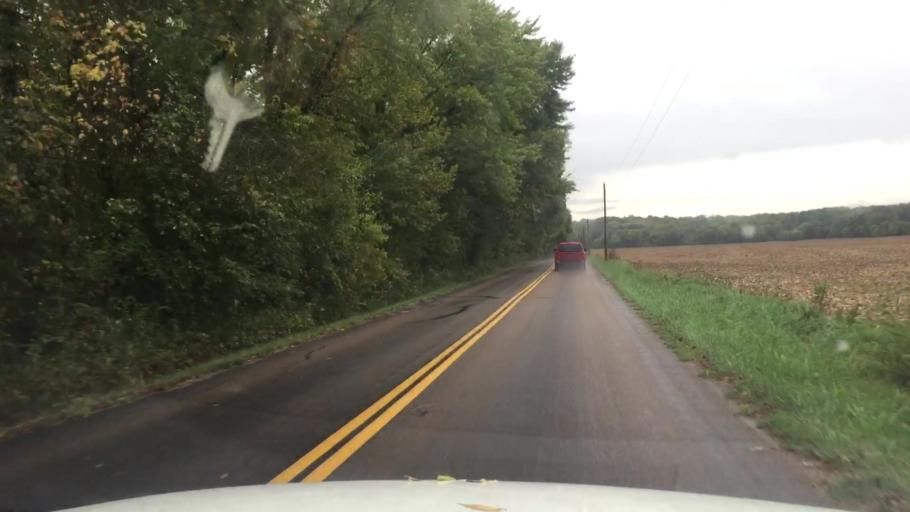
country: US
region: Missouri
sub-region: Boone County
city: Columbia
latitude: 38.9016
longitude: -92.4629
